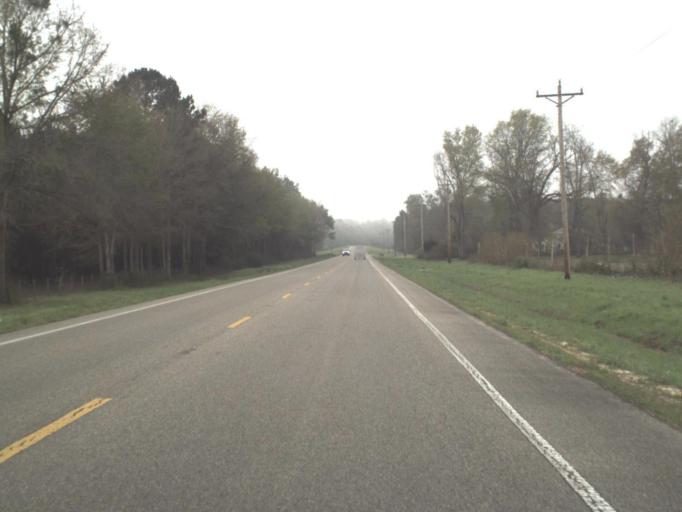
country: US
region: Florida
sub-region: Gadsden County
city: Gretna
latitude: 30.5766
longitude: -84.6730
